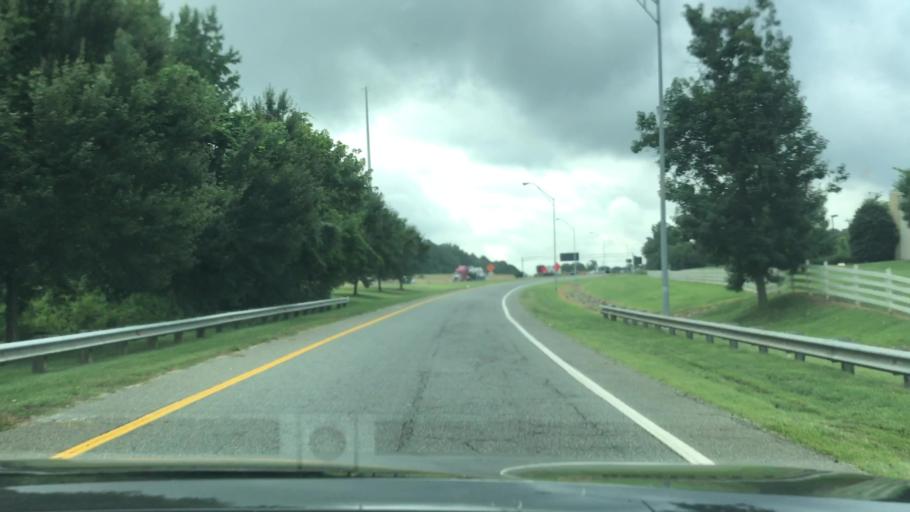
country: US
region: North Carolina
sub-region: Mecklenburg County
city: Huntersville
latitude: 35.4411
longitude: -80.8704
